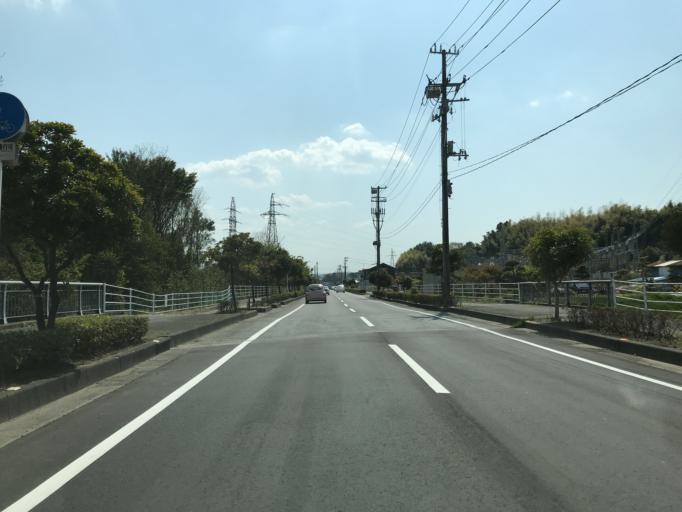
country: JP
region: Ibaraki
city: Kitaibaraki
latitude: 36.9049
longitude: 140.7710
